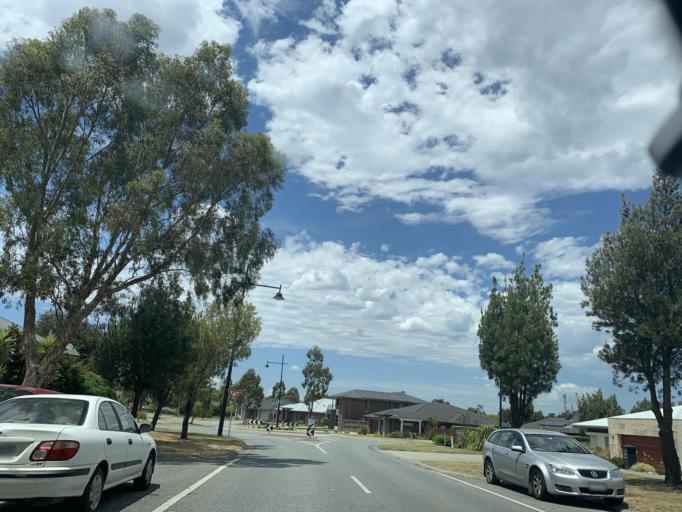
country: AU
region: Victoria
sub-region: Casey
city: Cranbourne South
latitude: -38.1463
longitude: 145.2522
